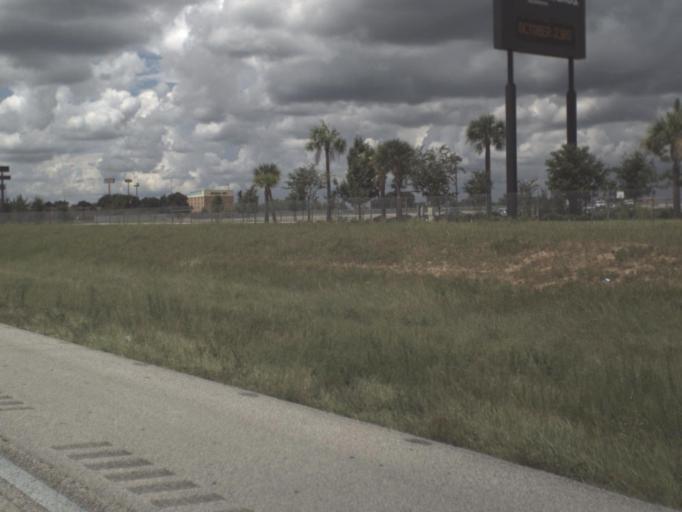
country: US
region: Florida
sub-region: Polk County
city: Loughman
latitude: 28.2371
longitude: -81.6442
